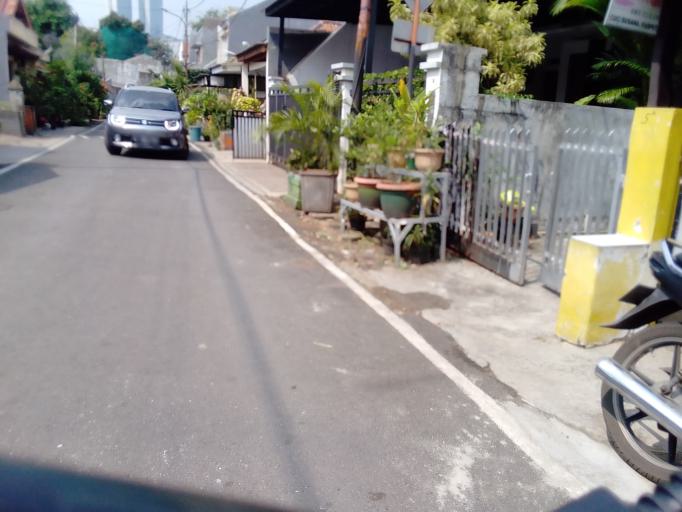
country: ID
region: Jakarta Raya
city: Jakarta
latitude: -6.2059
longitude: 106.8084
